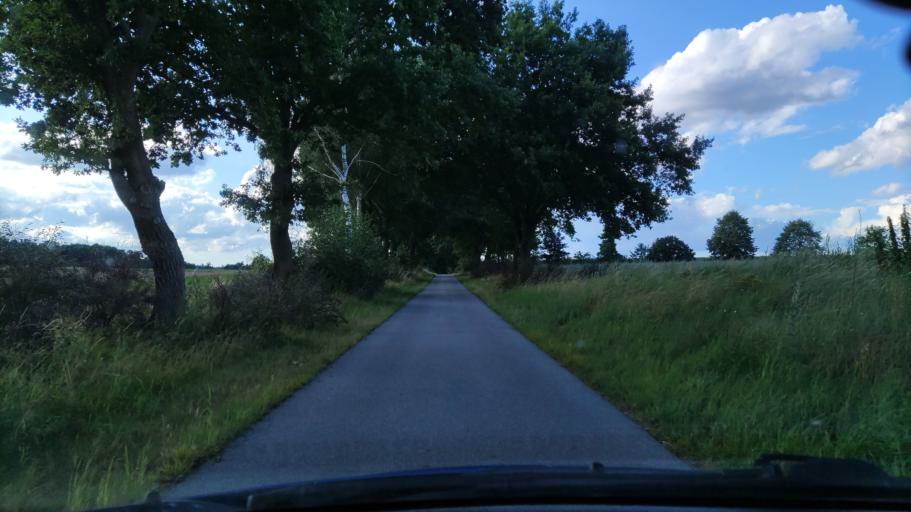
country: DE
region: Lower Saxony
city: Dahlenburg
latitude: 53.1818
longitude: 10.6887
